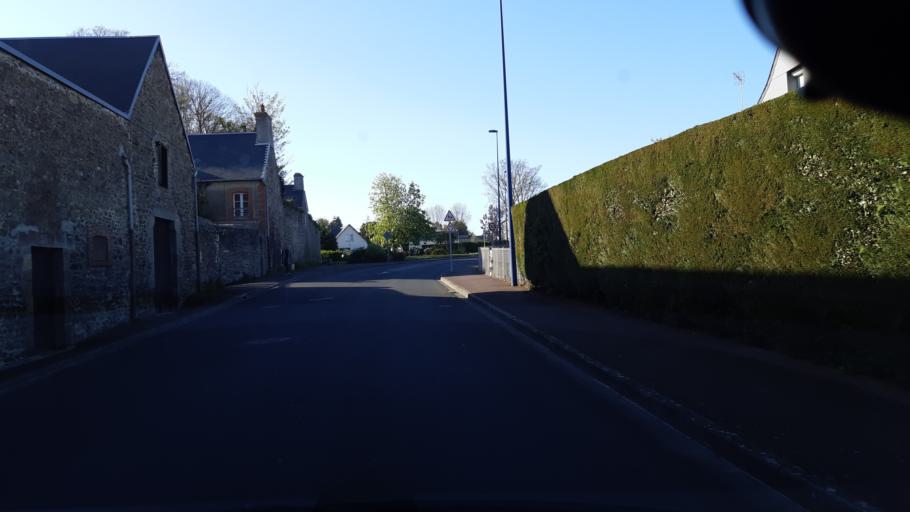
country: FR
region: Lower Normandy
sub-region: Departement de la Manche
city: Donville-les-Bains
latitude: 48.8323
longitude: -1.5830
